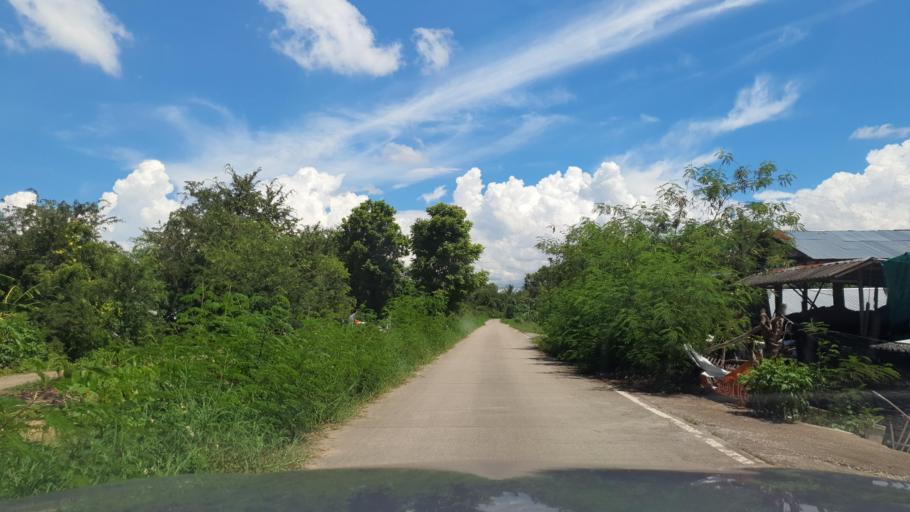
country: TH
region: Chiang Mai
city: San Kamphaeng
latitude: 18.7332
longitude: 99.1181
